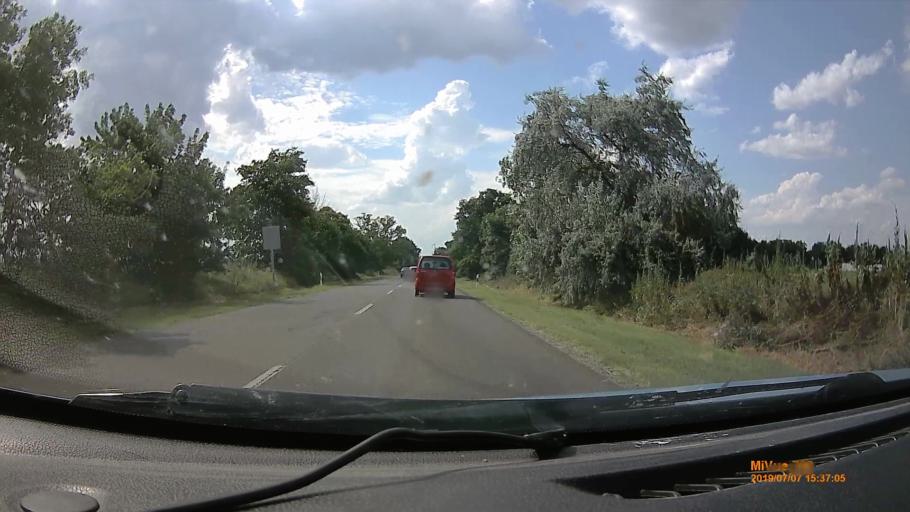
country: HU
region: Jasz-Nagykun-Szolnok
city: Jaszbereny
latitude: 47.4835
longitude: 19.9532
